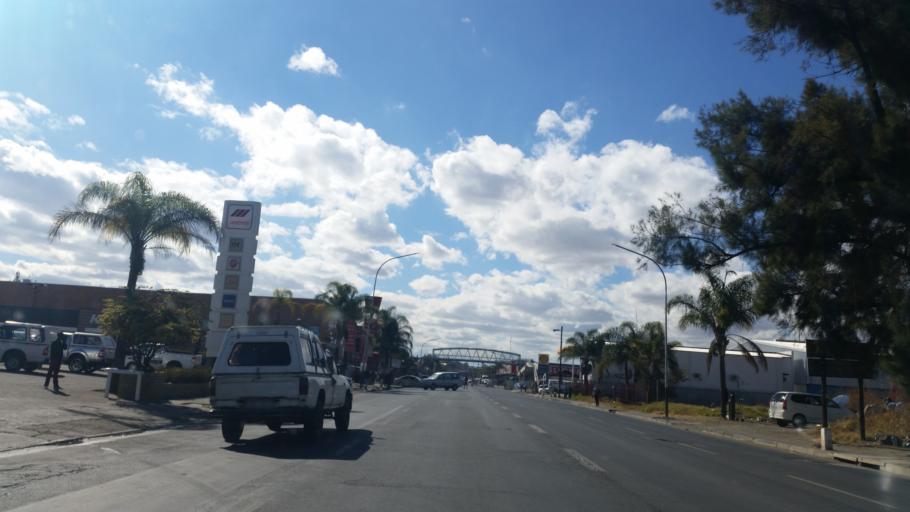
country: ZA
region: KwaZulu-Natal
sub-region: uThukela District Municipality
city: Ladysmith
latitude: -28.5624
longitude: 29.7816
